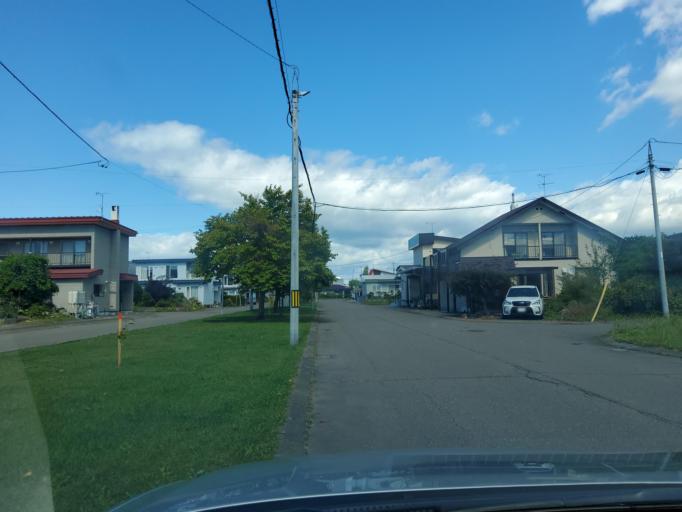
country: JP
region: Hokkaido
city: Otofuke
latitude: 42.9556
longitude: 143.2033
